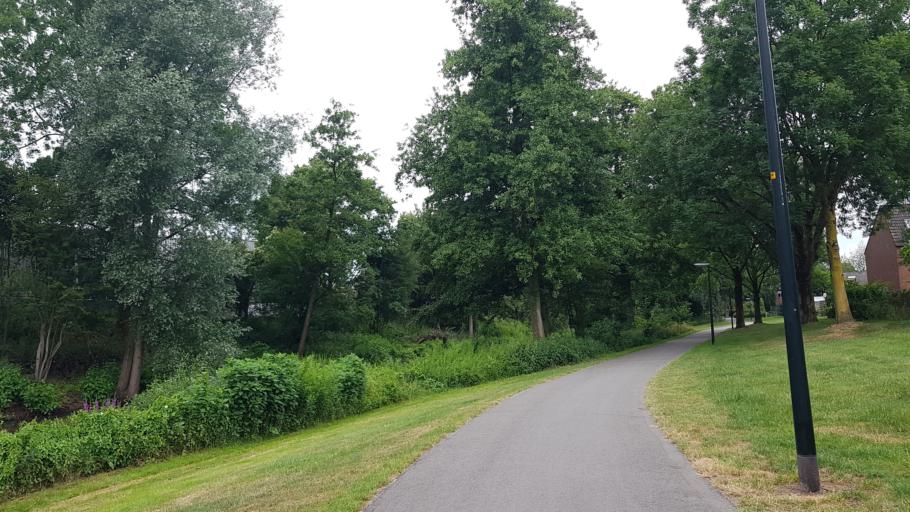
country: NL
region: Gelderland
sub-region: Gemeente Apeldoorn
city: Apeldoorn
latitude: 52.1871
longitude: 5.9947
